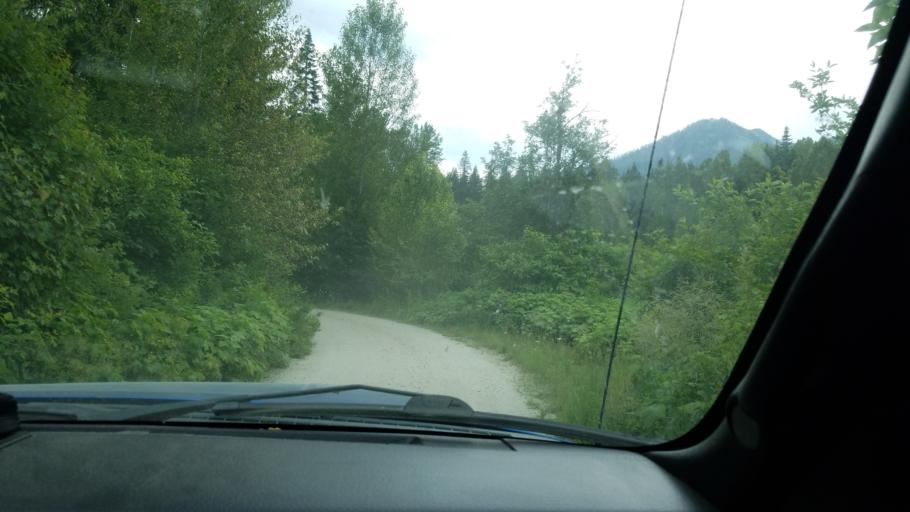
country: US
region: Washington
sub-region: Chelan County
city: Leavenworth
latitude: 47.9241
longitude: -120.9017
